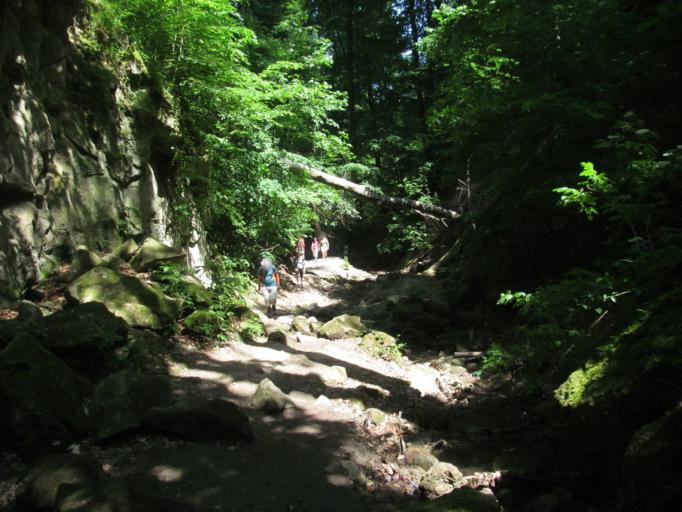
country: HU
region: Komarom-Esztergom
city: Pilismarot
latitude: 47.7399
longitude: 18.8942
